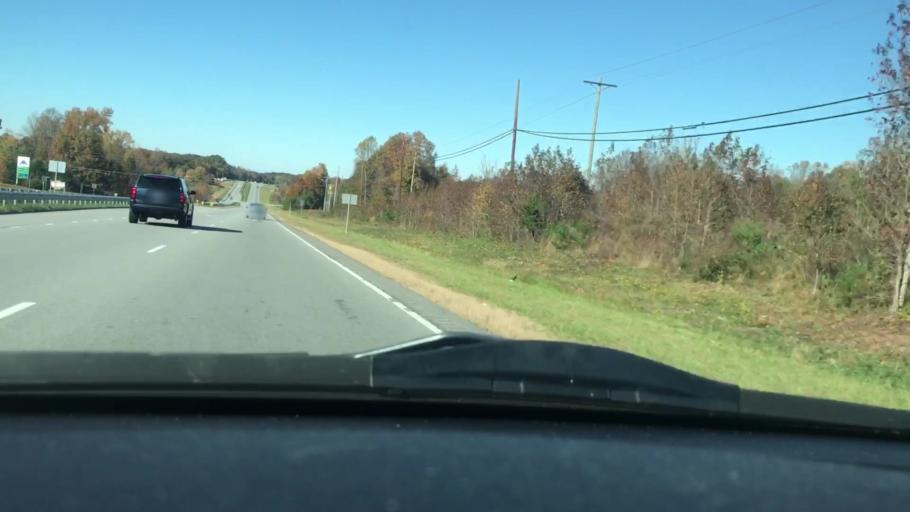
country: US
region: North Carolina
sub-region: Rockingham County
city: Madison
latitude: 36.3159
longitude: -79.9431
